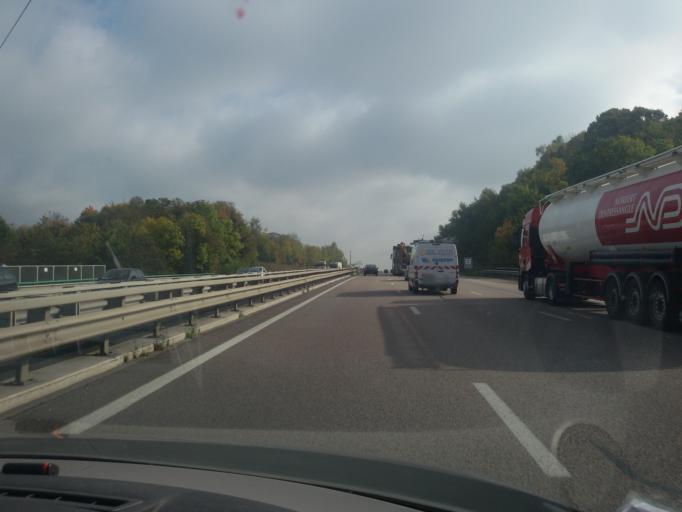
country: FR
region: Haute-Normandie
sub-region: Departement de la Seine-Maritime
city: Oissel
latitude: 49.3242
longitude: 1.0965
